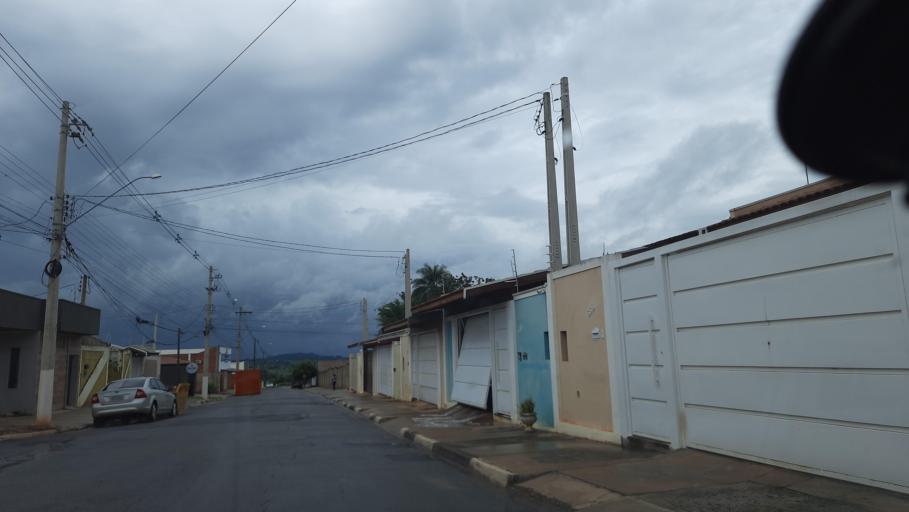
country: BR
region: Sao Paulo
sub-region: Casa Branca
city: Casa Branca
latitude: -21.7763
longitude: -47.0974
